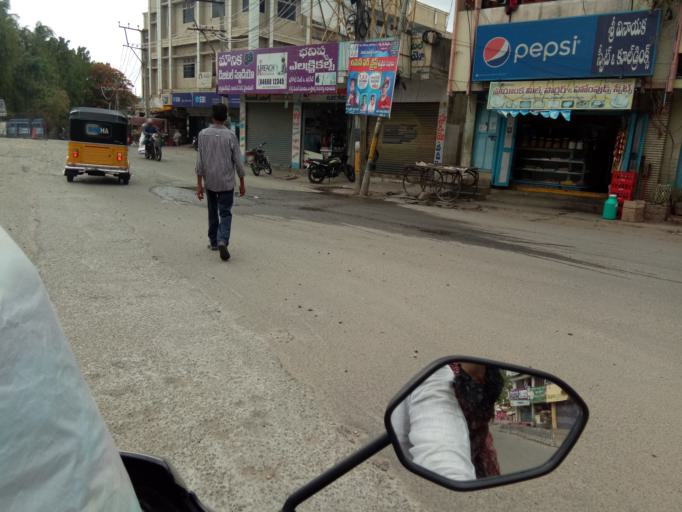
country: IN
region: Telangana
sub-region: Khammam
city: Khammam
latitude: 17.2402
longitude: 80.1433
